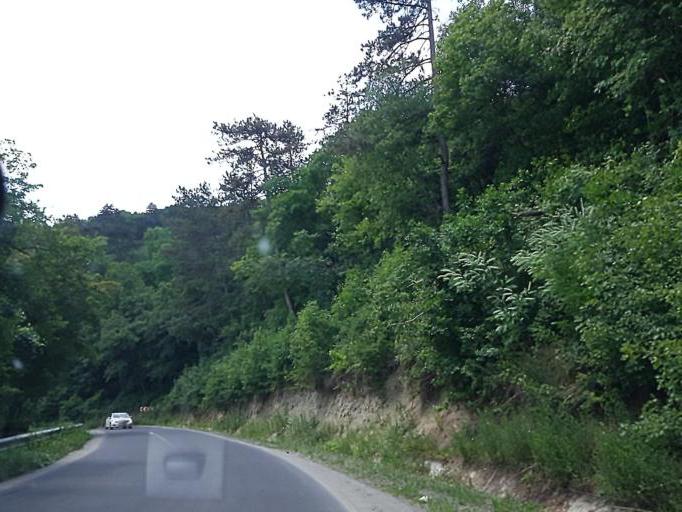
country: RO
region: Sibiu
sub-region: Comuna Seica Mare
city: Seica Mare
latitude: 46.0363
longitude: 24.1600
